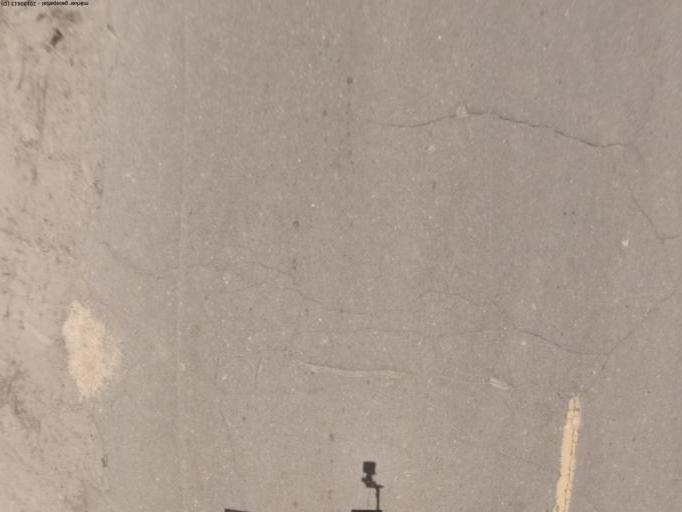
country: US
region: California
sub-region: Madera County
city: Chowchilla
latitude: 37.0498
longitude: -120.2926
